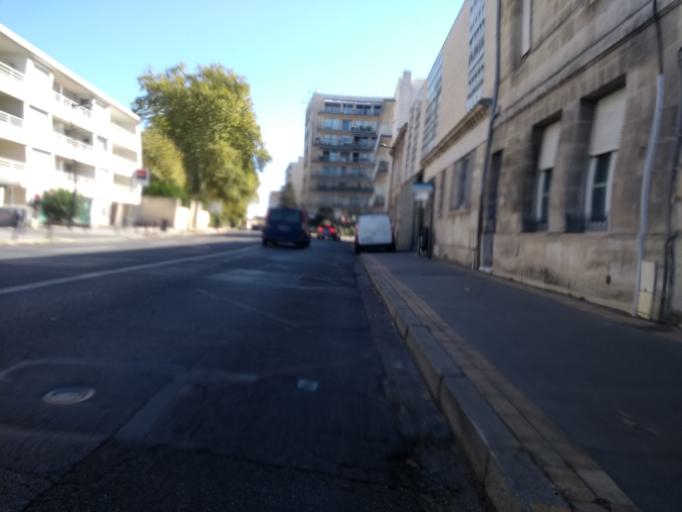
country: FR
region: Aquitaine
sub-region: Departement de la Gironde
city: Le Bouscat
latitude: 44.8502
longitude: -0.6053
